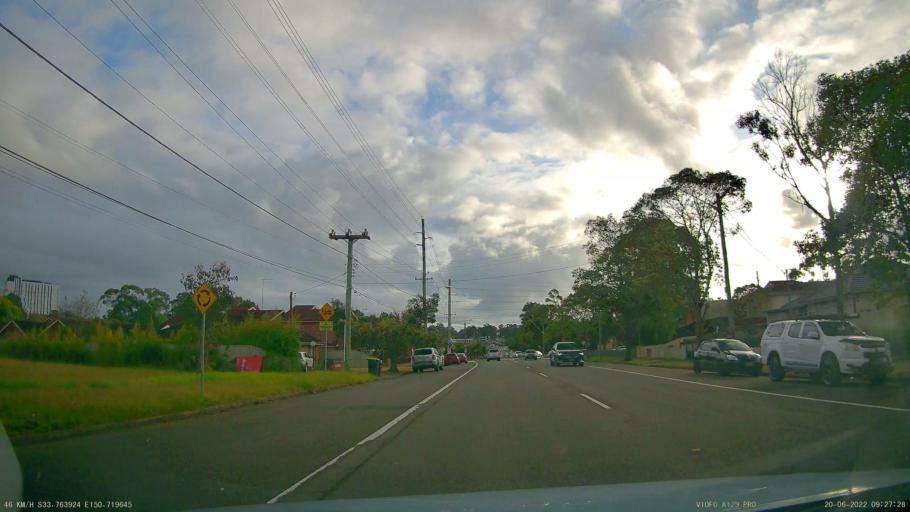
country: AU
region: New South Wales
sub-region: Penrith Municipality
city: Kingswood Park
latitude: -33.7637
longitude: 150.7197
